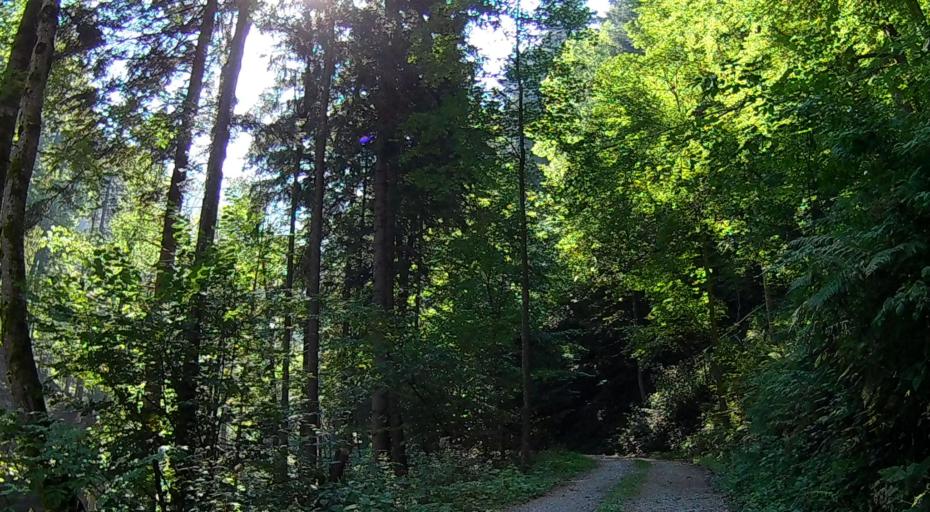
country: SI
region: Selnica ob Dravi
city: Selnica ob Dravi
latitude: 46.5163
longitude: 15.4561
